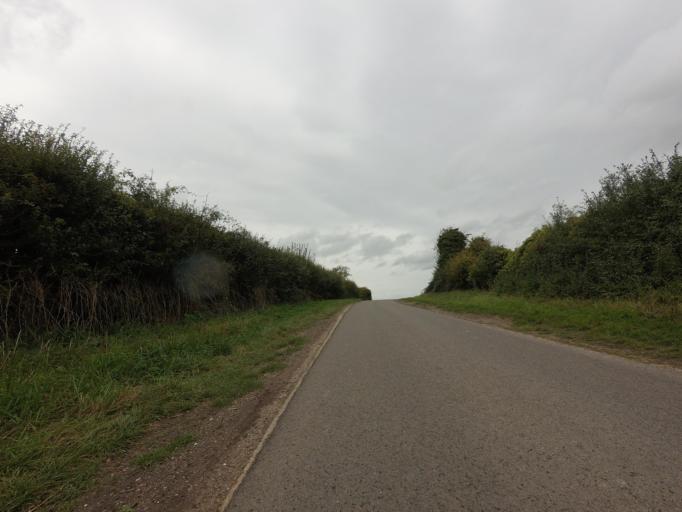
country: GB
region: England
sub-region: Cambridgeshire
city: Duxford
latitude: 52.0497
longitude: 0.1371
